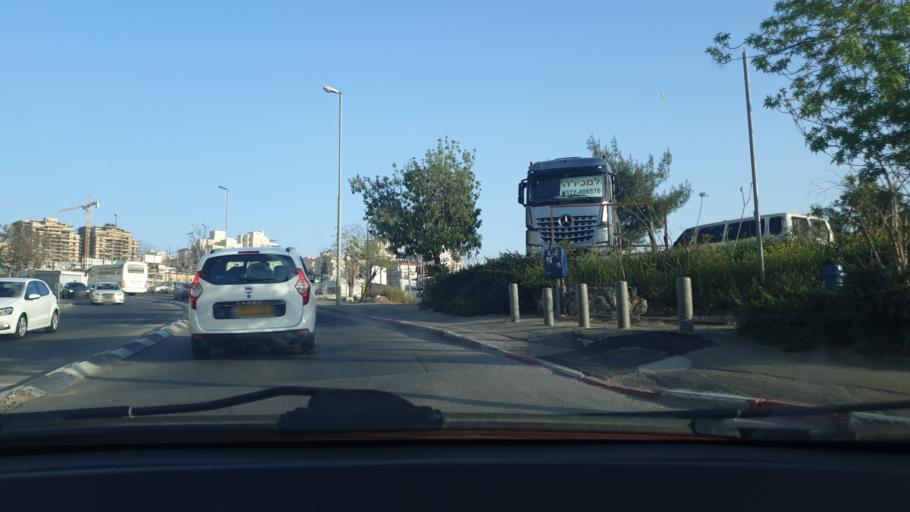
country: PS
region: West Bank
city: Bayt Iksa
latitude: 31.7938
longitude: 35.1870
